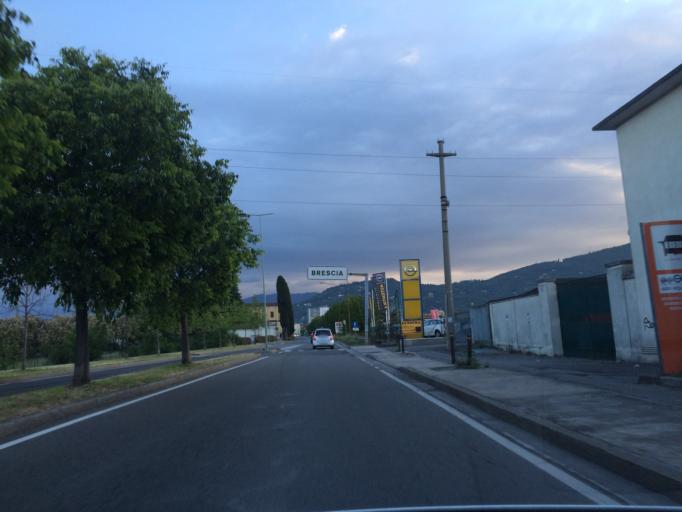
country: IT
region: Lombardy
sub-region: Provincia di Brescia
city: Brescia
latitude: 45.5153
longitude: 10.2274
